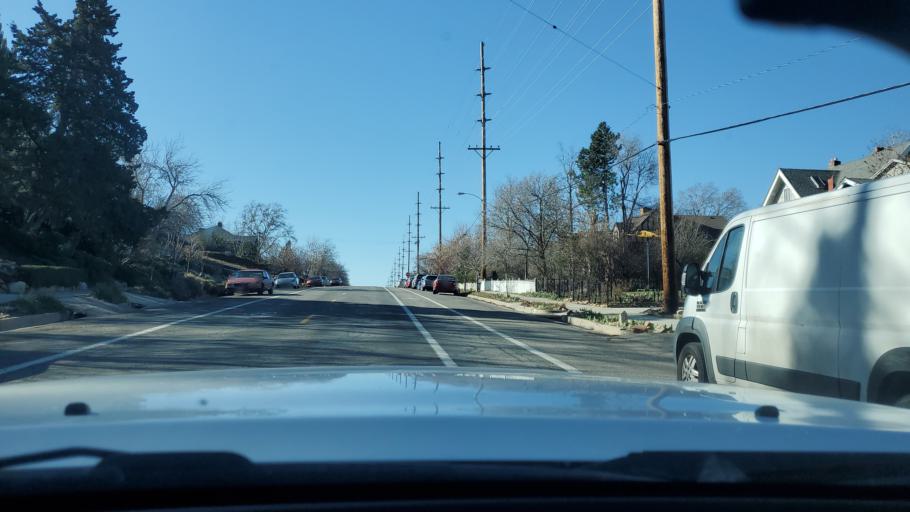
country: US
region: Utah
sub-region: Salt Lake County
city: Salt Lake City
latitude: 40.7621
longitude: -111.8596
